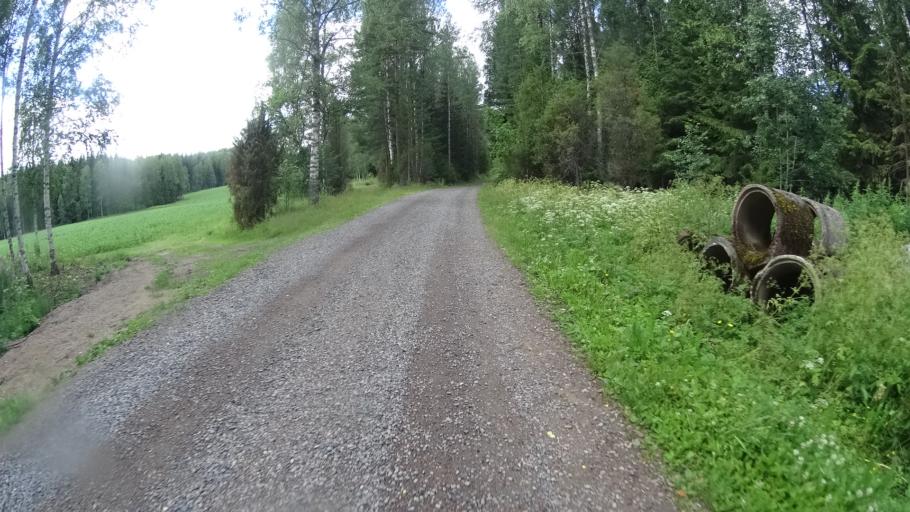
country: FI
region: Uusimaa
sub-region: Helsinki
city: Karkkila
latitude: 60.6029
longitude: 24.2043
